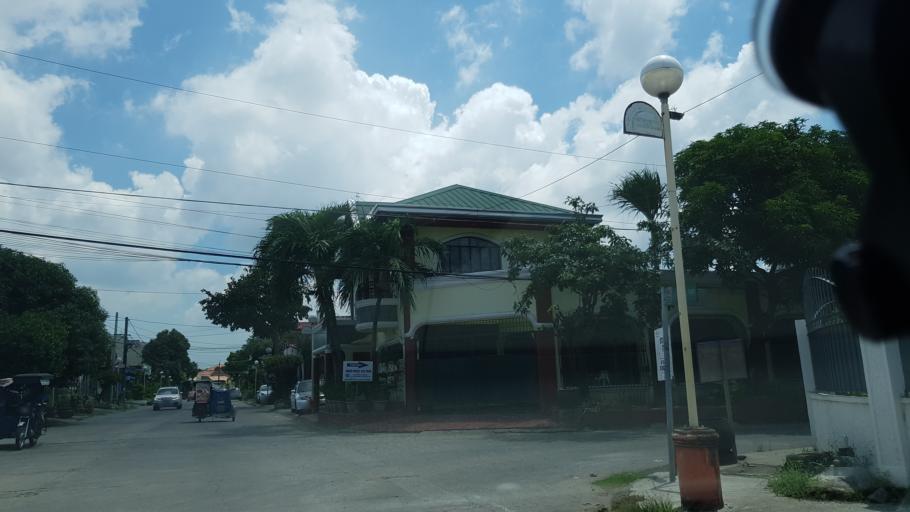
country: PH
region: Calabarzon
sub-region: Province of Rizal
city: Las Pinas
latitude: 14.4353
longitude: 120.9817
